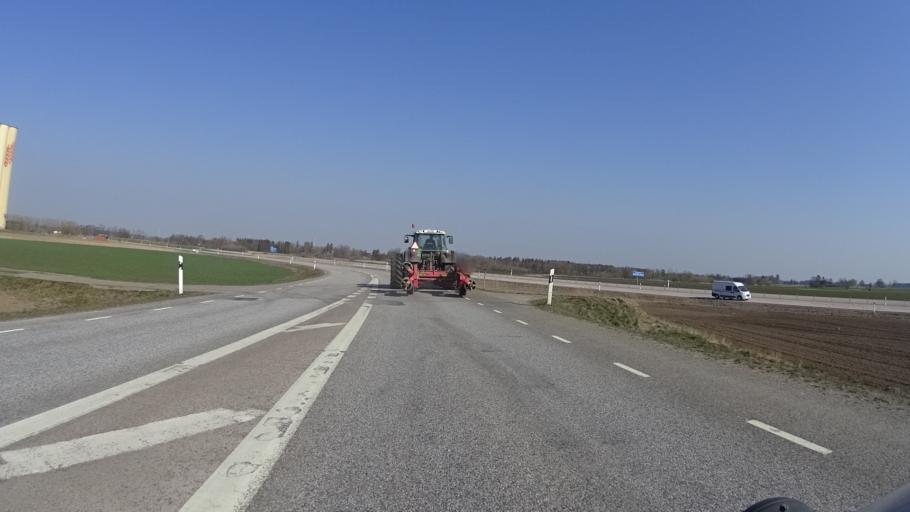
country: SE
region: OEstergoetland
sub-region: Mjolby Kommun
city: Mjolby
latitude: 58.3948
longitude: 15.1042
